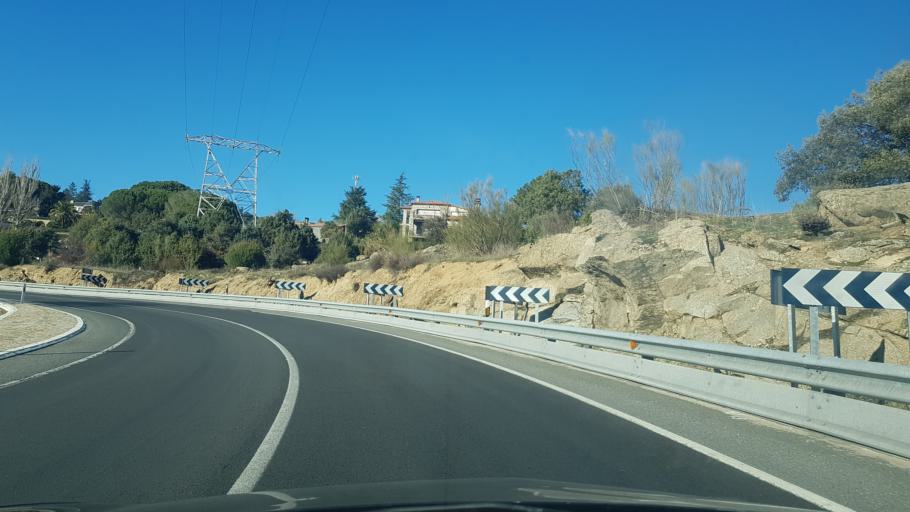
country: ES
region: Castille and Leon
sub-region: Provincia de Avila
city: El Tiemblo
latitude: 40.4357
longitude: -4.5522
